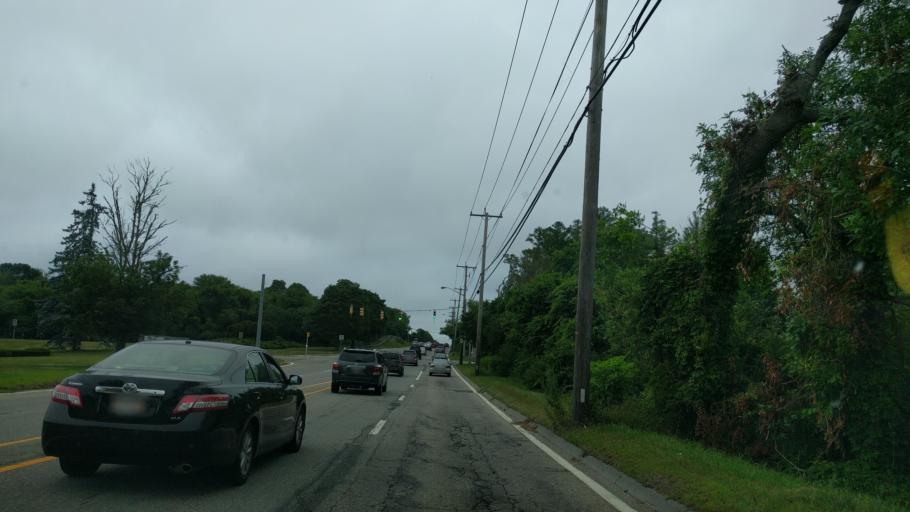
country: US
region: Rhode Island
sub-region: Newport County
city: Melville
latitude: 41.5696
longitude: -71.2776
